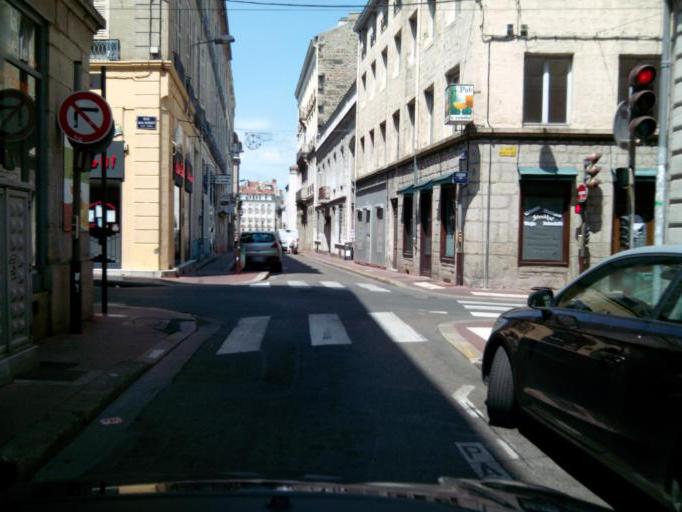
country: FR
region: Rhone-Alpes
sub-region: Departement de la Loire
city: Saint-Etienne
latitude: 45.4375
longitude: 4.3851
